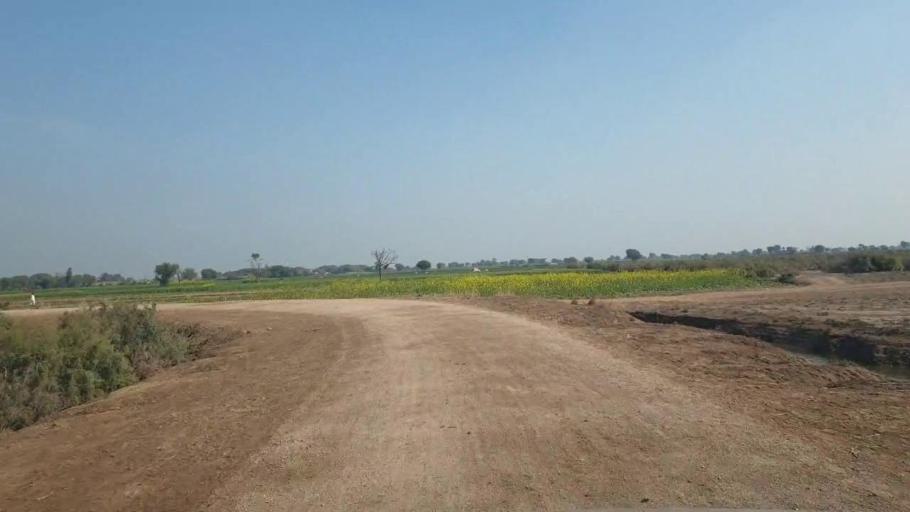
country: PK
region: Sindh
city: Shahdadpur
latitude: 25.9830
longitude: 68.5141
